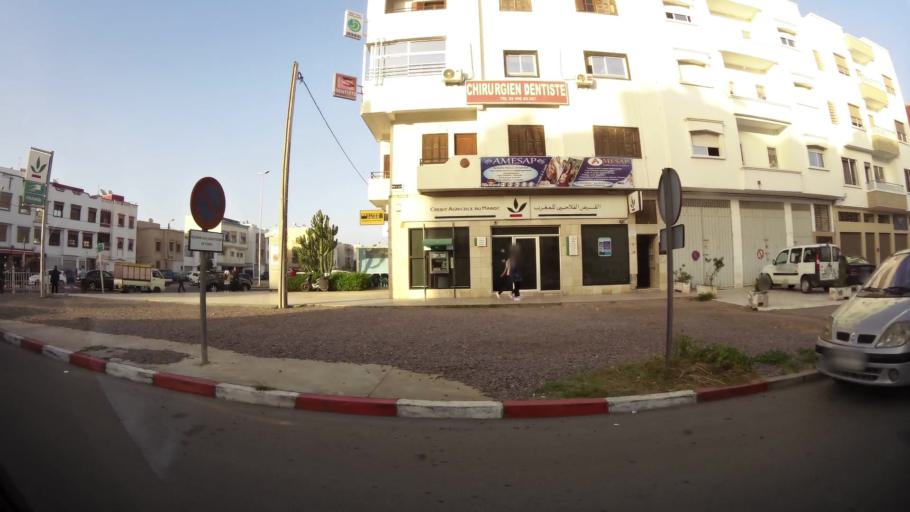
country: MA
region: Oued ed Dahab-Lagouira
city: Dakhla
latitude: 30.3957
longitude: -9.5466
